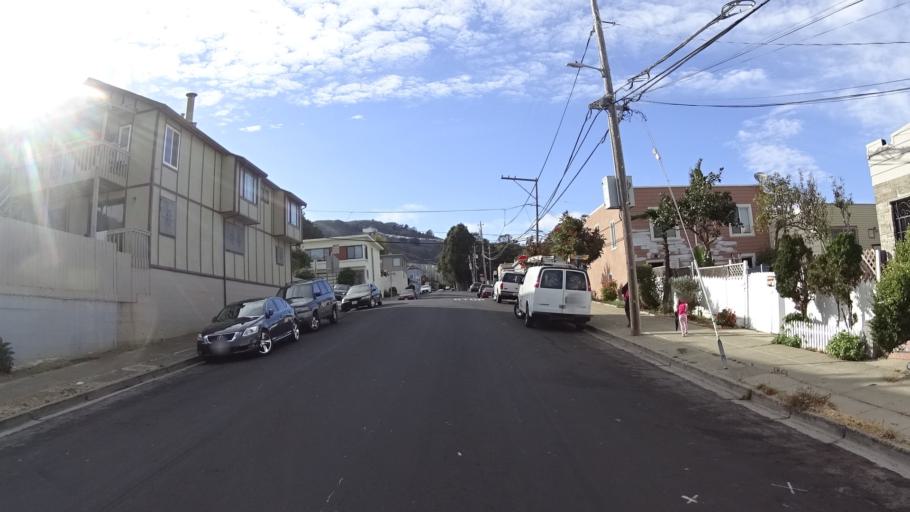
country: US
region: California
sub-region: San Mateo County
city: Brisbane
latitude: 37.7015
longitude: -122.4167
